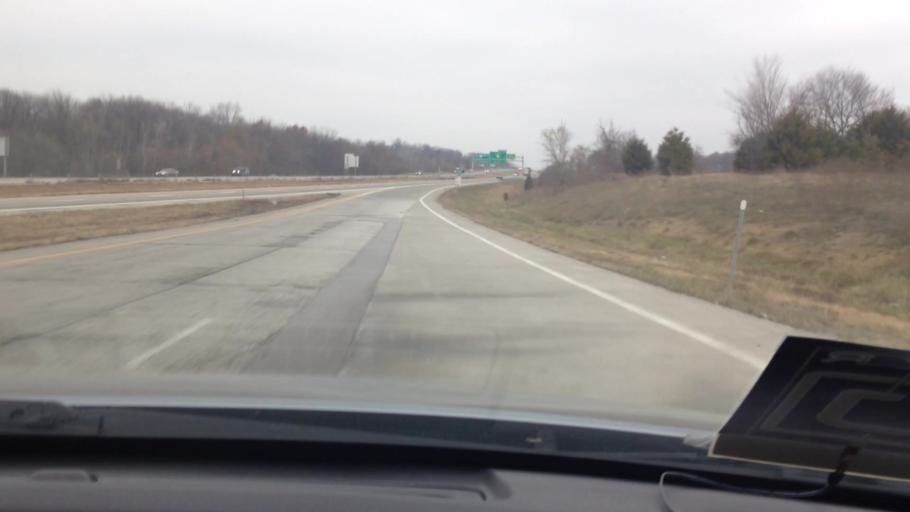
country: US
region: Missouri
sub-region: Cass County
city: Harrisonville
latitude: 38.6186
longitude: -94.3482
